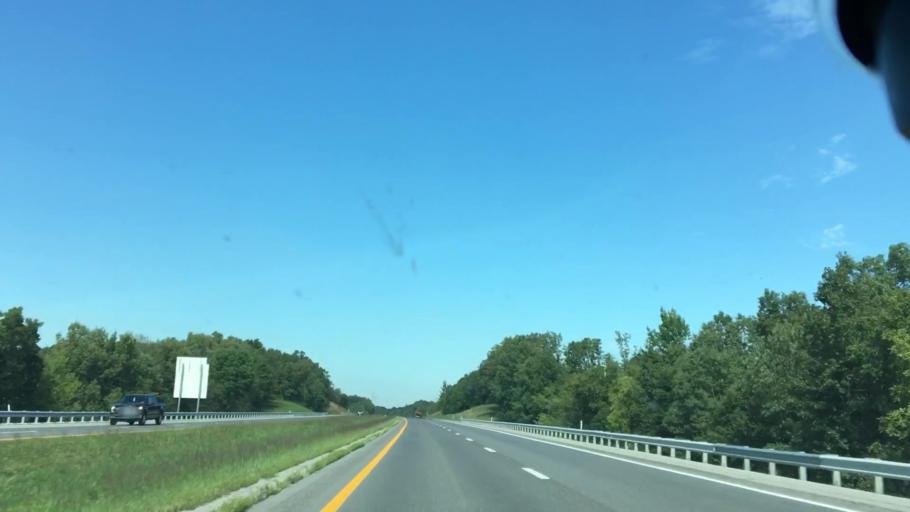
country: US
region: Kentucky
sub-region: Webster County
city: Sebree
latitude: 37.5167
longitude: -87.4748
